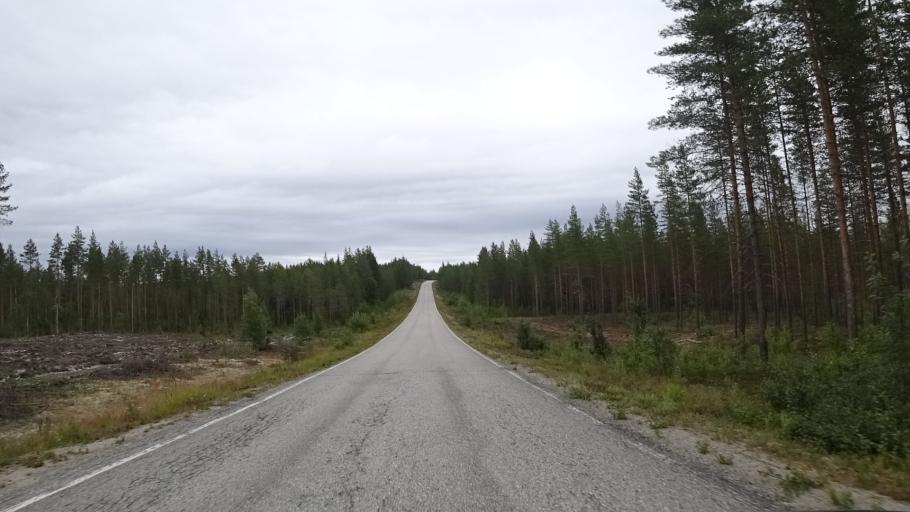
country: FI
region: North Karelia
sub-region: Pielisen Karjala
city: Lieksa
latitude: 63.3797
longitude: 30.3167
